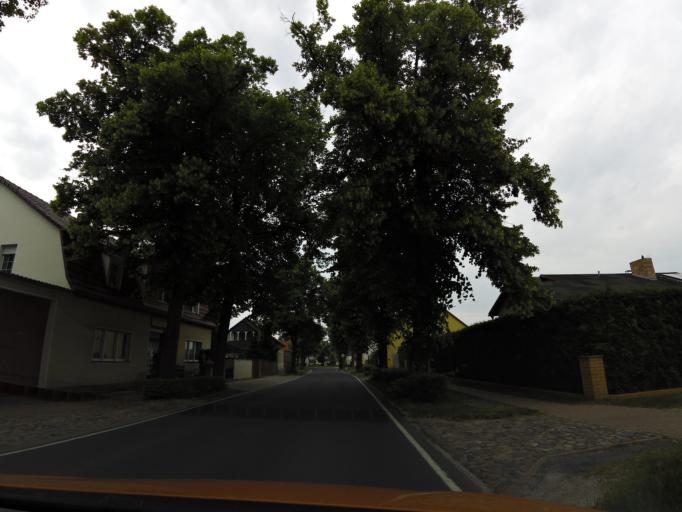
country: DE
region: Brandenburg
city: Rangsdorf
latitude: 52.2531
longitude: 13.3789
